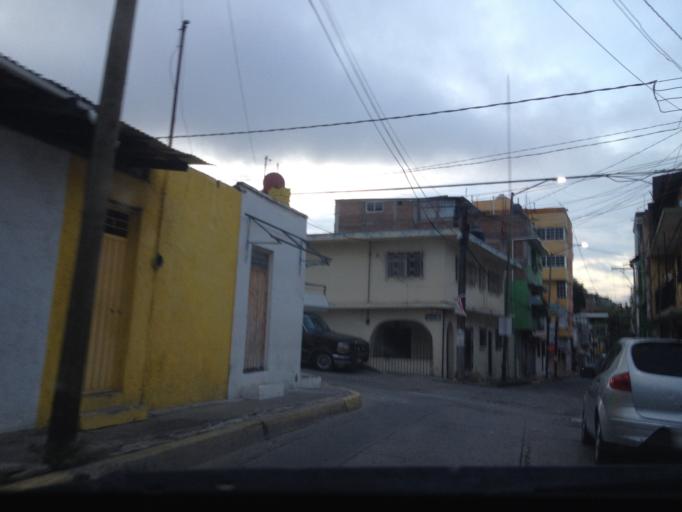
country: MX
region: Guerrero
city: Chilpancingo de los Bravos
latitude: 17.5598
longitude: -99.5026
